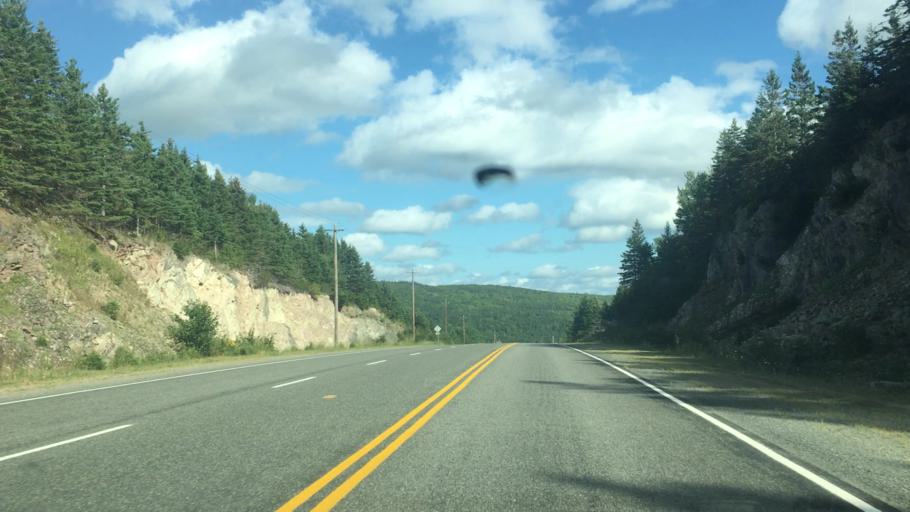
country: CA
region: Nova Scotia
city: Sydney
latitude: 45.8145
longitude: -60.6839
